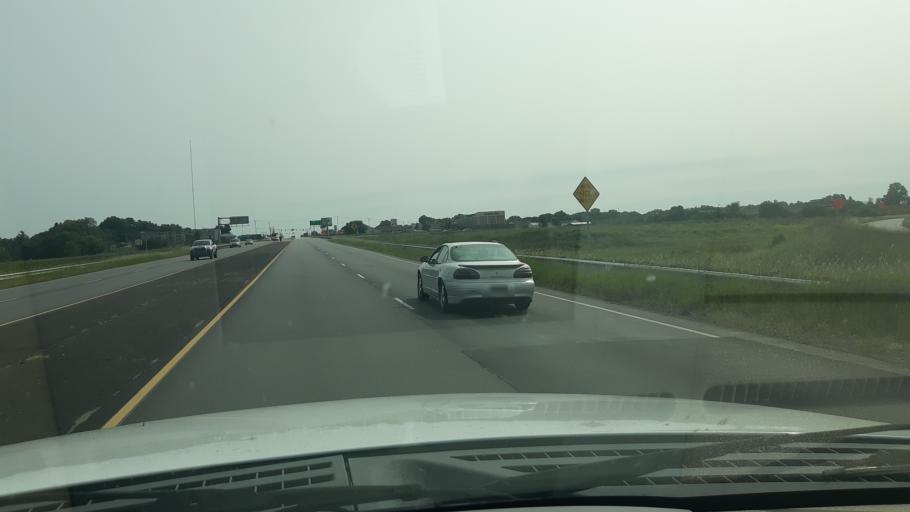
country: US
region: Indiana
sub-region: Gibson County
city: Princeton
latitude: 38.3554
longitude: -87.6020
